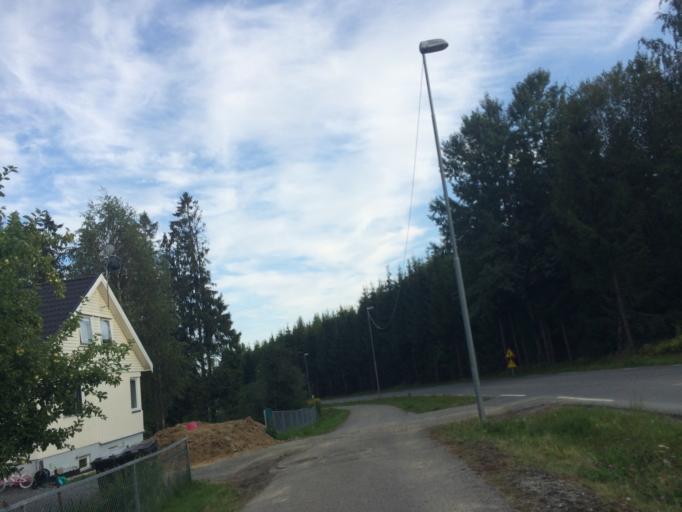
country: NO
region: Akershus
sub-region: Ski
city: Ski
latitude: 59.6996
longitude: 10.8464
